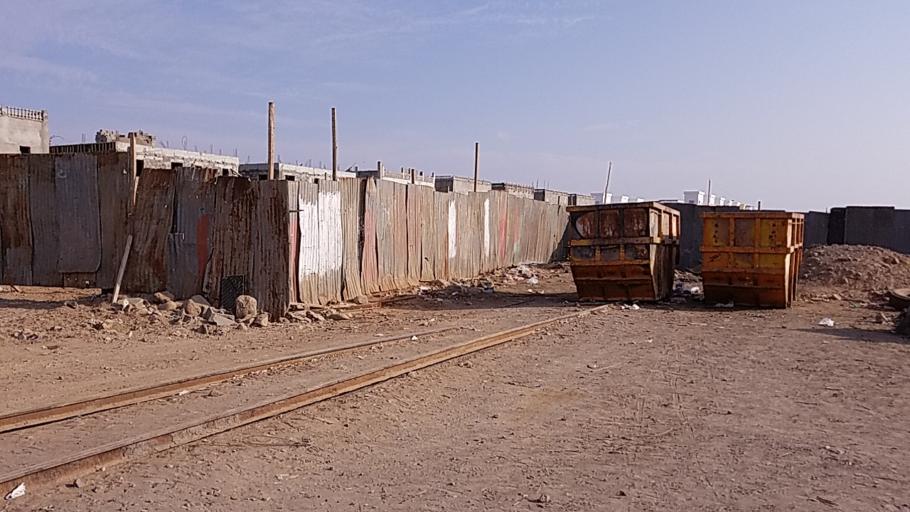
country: DJ
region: Djibouti
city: Djibouti
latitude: 11.5744
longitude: 43.1482
